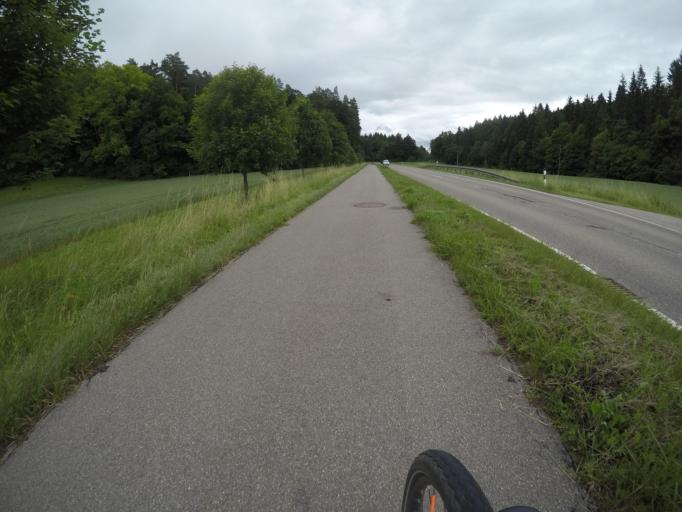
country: DE
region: Baden-Wuerttemberg
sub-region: Regierungsbezirk Stuttgart
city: Aidlingen
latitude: 48.6602
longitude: 8.8796
